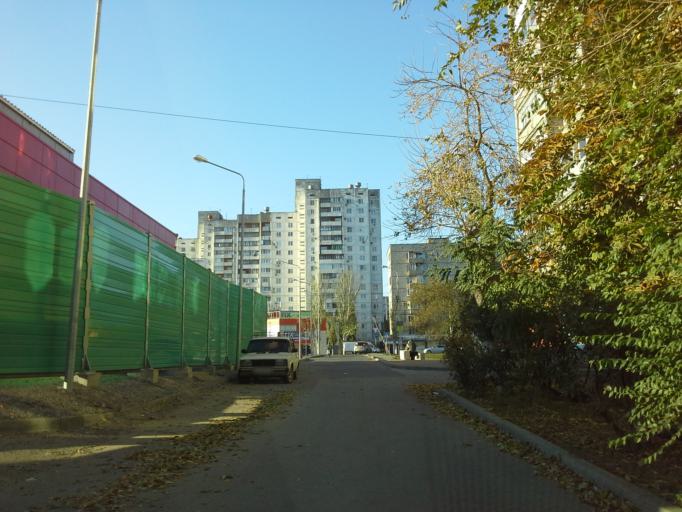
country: RU
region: Volgograd
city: Vodstroy
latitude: 48.8205
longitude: 44.6370
